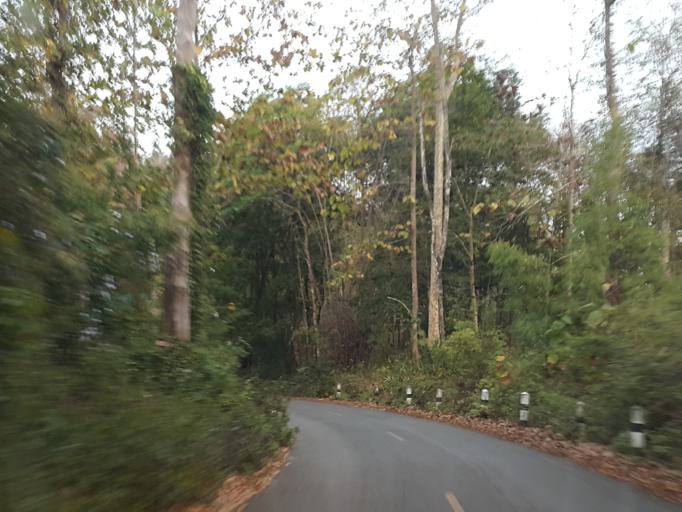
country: TH
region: Lampang
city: Mueang Pan
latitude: 18.8283
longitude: 99.4617
